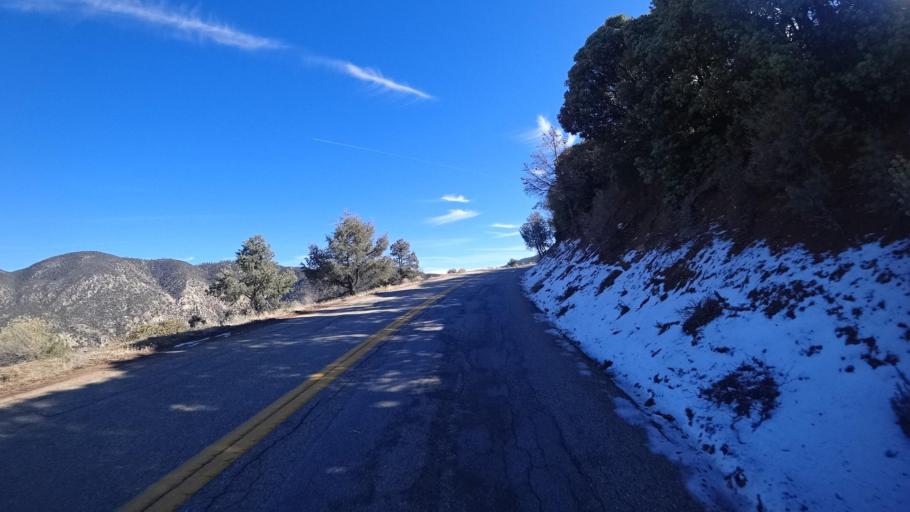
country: US
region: California
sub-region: Kern County
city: Pine Mountain Club
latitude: 34.8667
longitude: -119.2555
